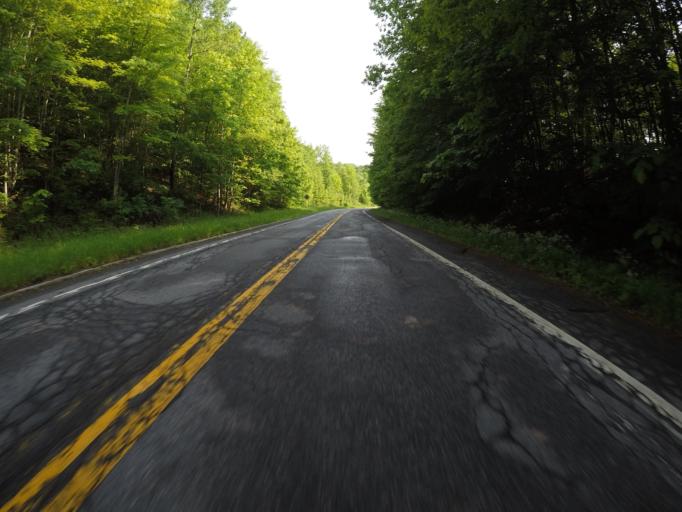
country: US
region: New York
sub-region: Sullivan County
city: Livingston Manor
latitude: 42.1192
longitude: -74.7426
